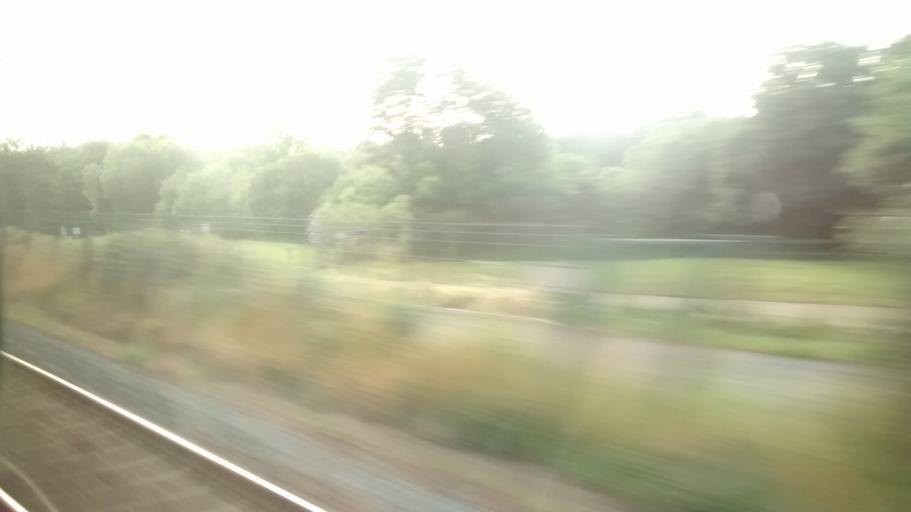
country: FR
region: Brittany
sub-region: Departement d'Ille-et-Vilaine
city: Brece
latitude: 48.1111
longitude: -1.4781
